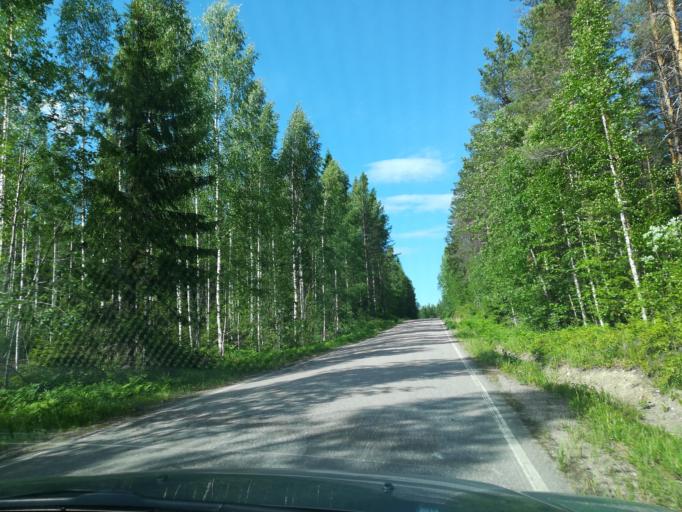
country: FI
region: South Karelia
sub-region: Imatra
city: Ruokolahti
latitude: 61.4801
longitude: 28.8737
